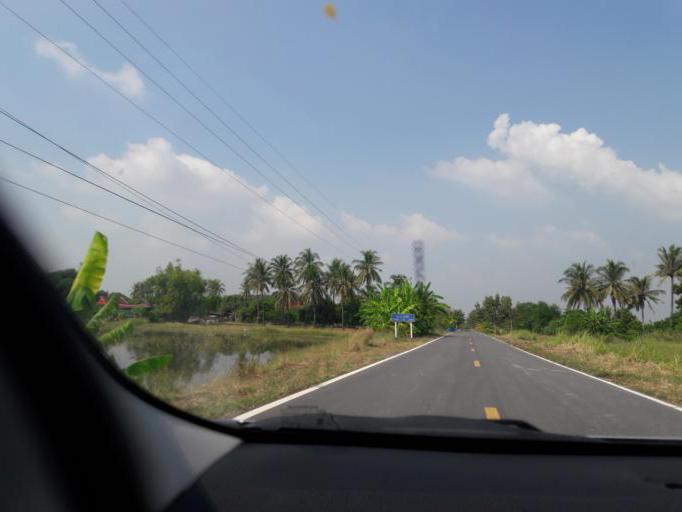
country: TH
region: Ang Thong
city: Wiset Chaichan
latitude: 14.5629
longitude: 100.3894
